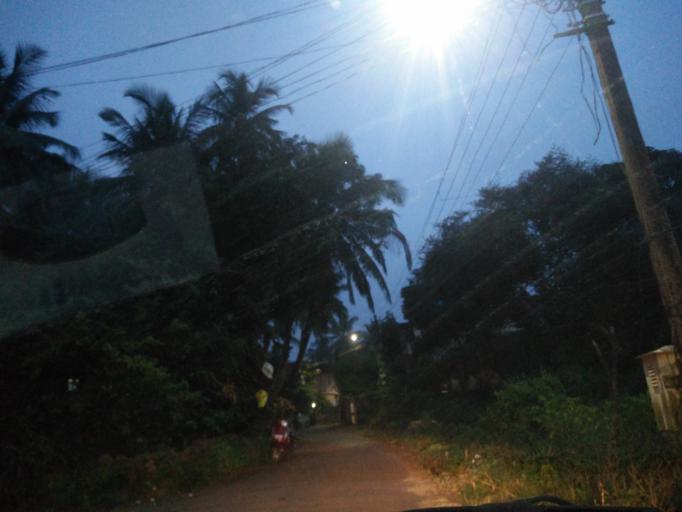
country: IN
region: Goa
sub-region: South Goa
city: Chinchinim
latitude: 15.2105
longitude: 73.9775
